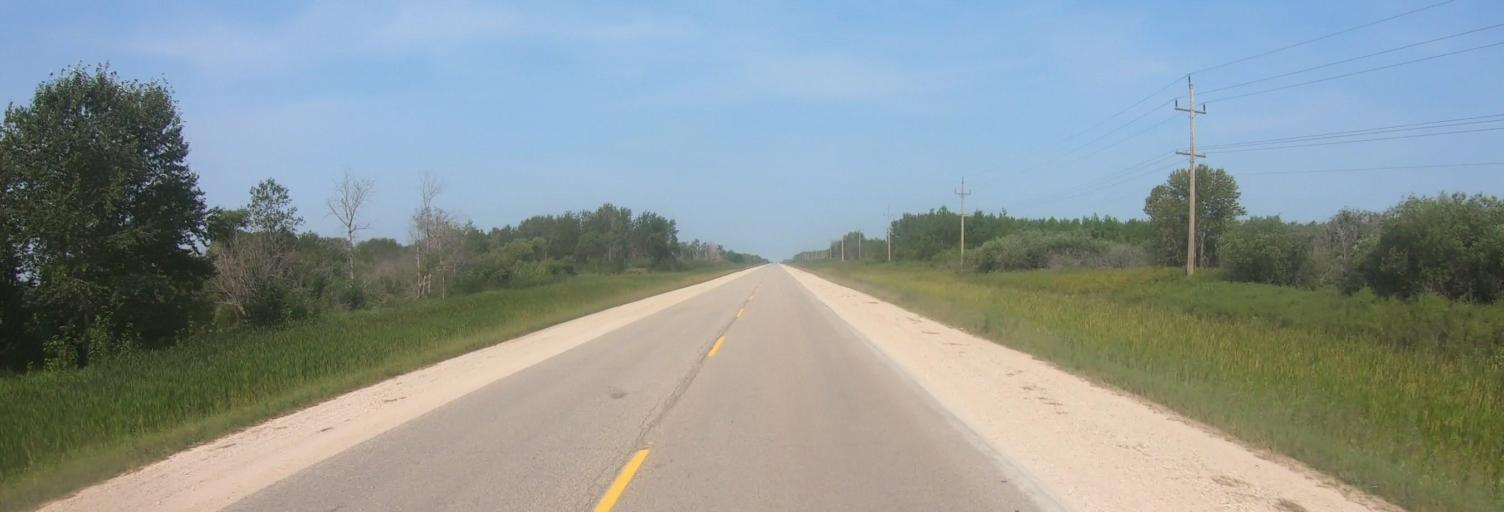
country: CA
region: Manitoba
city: La Broquerie
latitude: 49.2883
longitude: -96.5196
